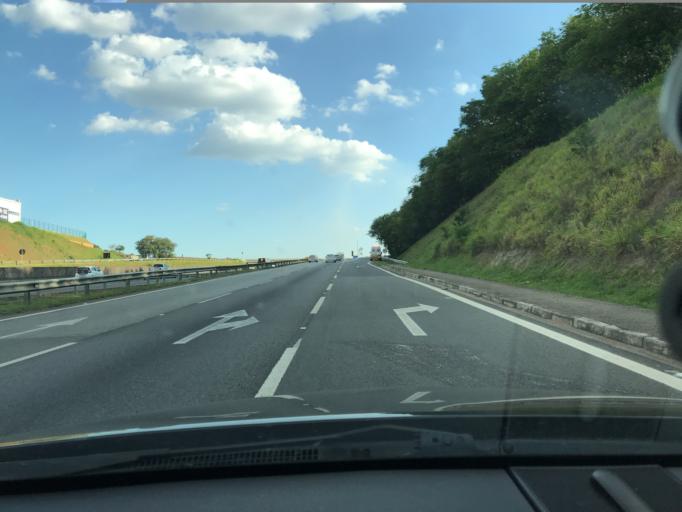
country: BR
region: Sao Paulo
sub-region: Valinhos
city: Valinhos
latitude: -22.9773
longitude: -47.0474
